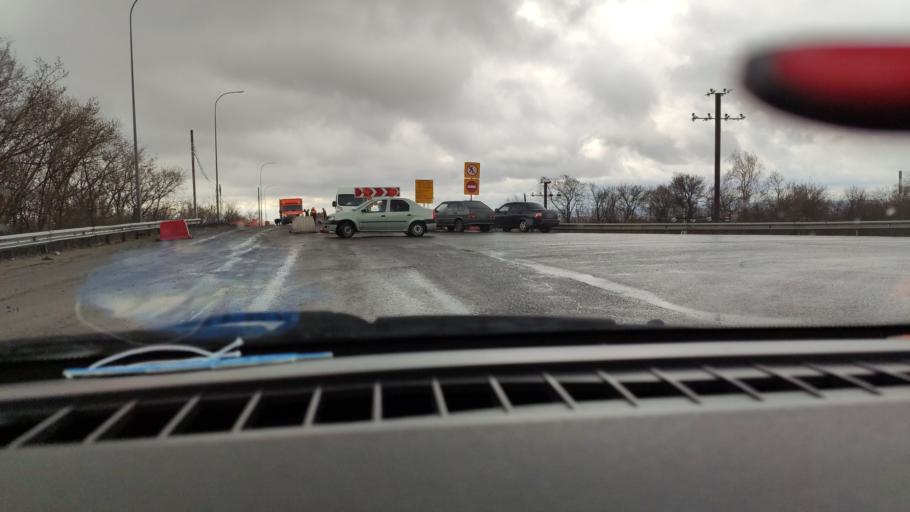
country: RU
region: Tatarstan
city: Nurlat
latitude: 54.4295
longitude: 50.8251
